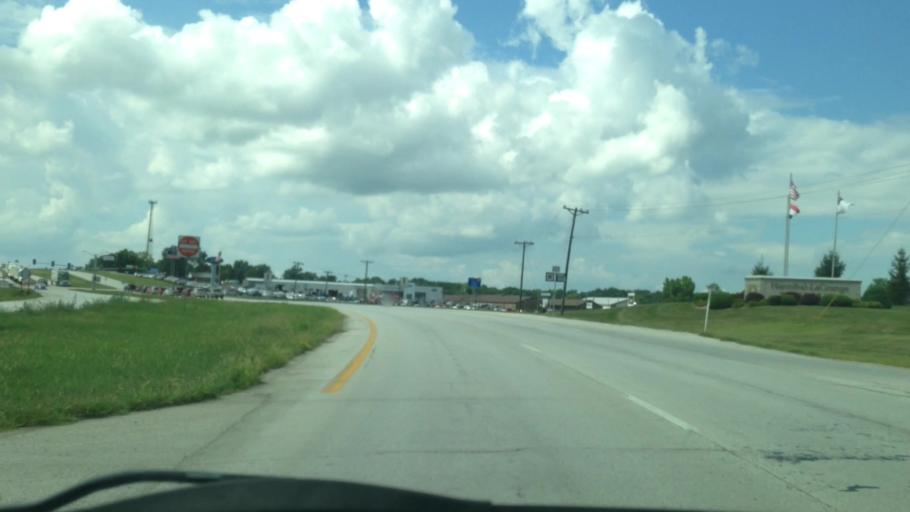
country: US
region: Missouri
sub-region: Marion County
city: Hannibal
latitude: 39.7269
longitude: -91.3924
